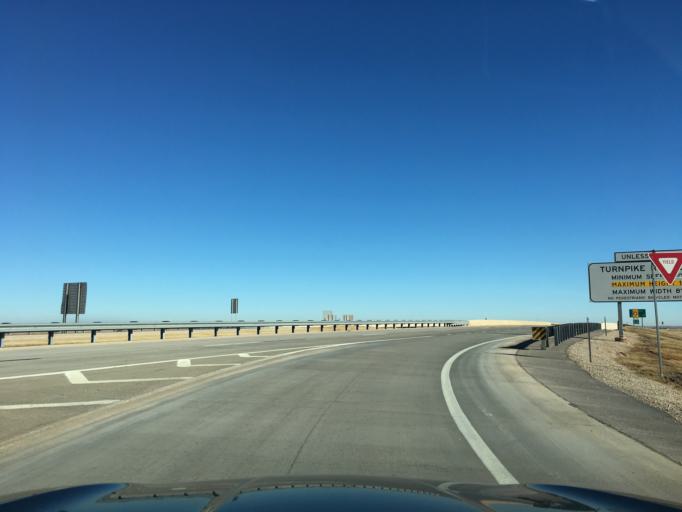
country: US
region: Oklahoma
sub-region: Noble County
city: Perry
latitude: 36.3999
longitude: -97.3284
